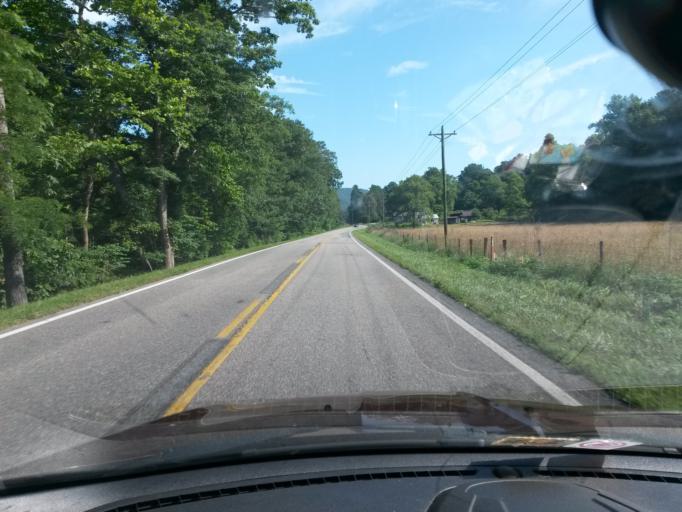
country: US
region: Virginia
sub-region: Shenandoah County
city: Basye
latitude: 38.7347
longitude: -78.9168
